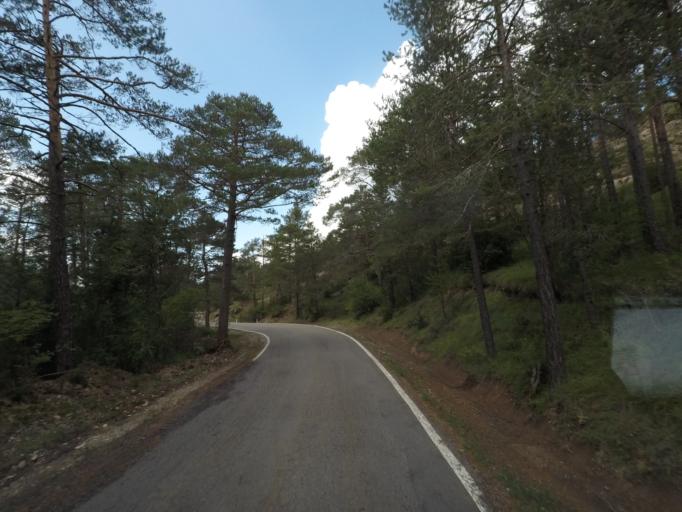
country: ES
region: Aragon
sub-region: Provincia de Huesca
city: Fiscal
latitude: 42.4058
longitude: -0.1740
